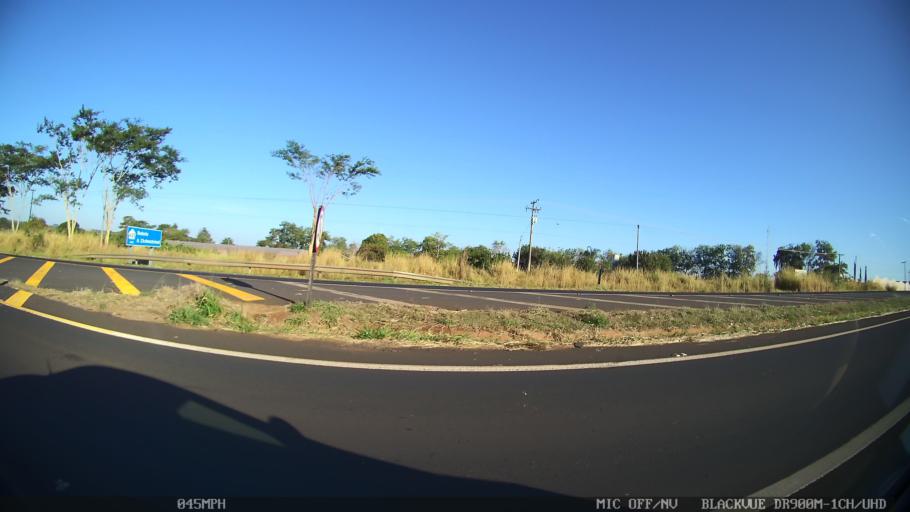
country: BR
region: Sao Paulo
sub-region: Guapiacu
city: Guapiacu
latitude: -20.7712
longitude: -49.2181
